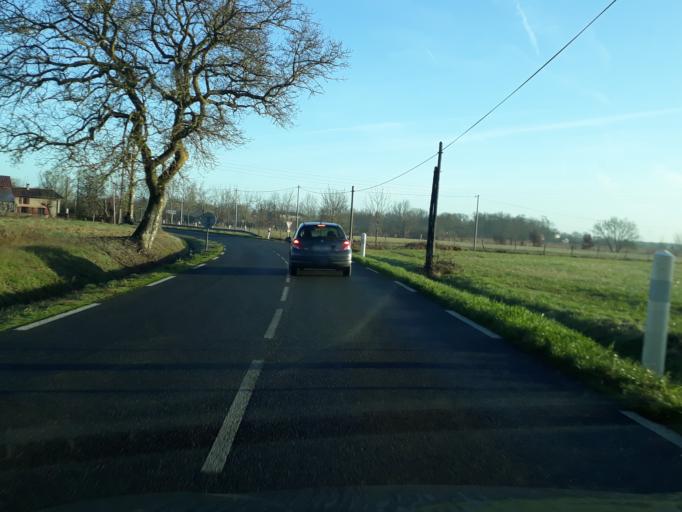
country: FR
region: Midi-Pyrenees
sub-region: Departement de la Haute-Garonne
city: Sainte-Foy-de-Peyrolieres
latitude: 43.4579
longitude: 1.1426
